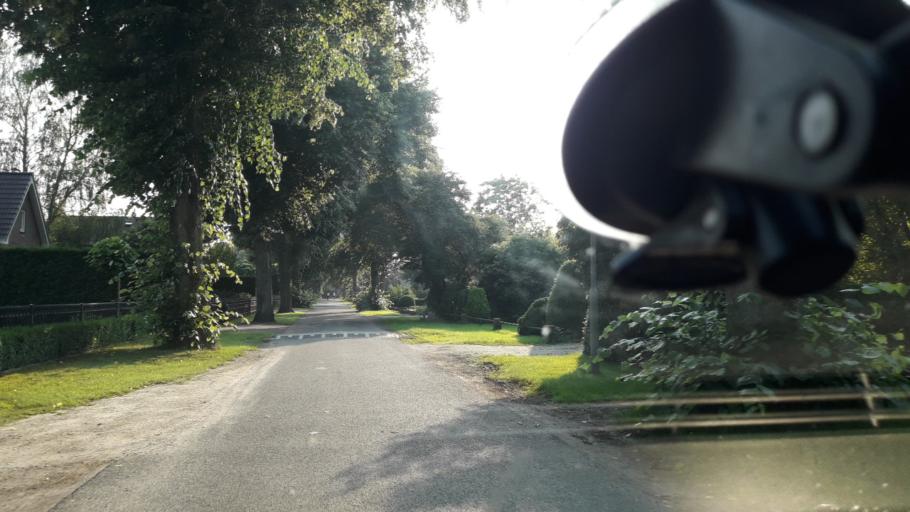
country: NL
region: Gelderland
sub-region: Gemeente Harderwijk
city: Harderwijk
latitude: 52.3595
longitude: 5.6861
